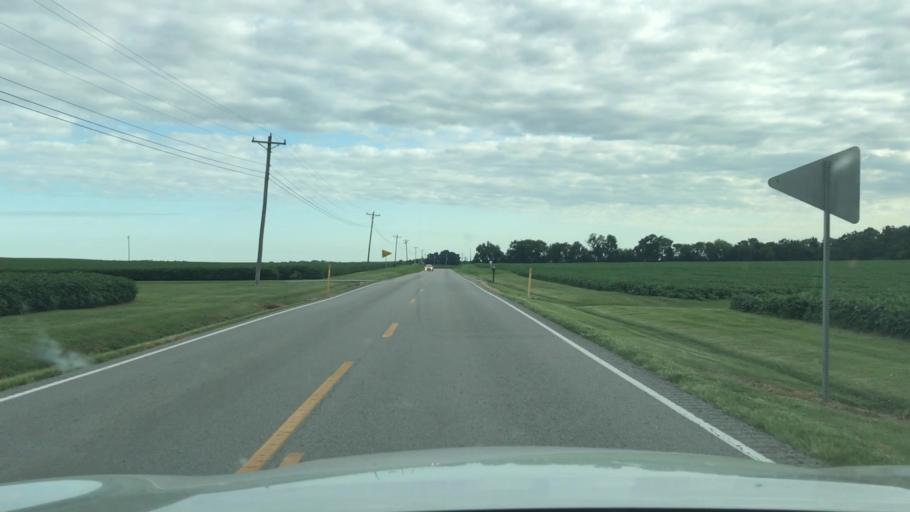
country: US
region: Kentucky
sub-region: Todd County
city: Elkton
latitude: 36.7666
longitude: -87.1669
